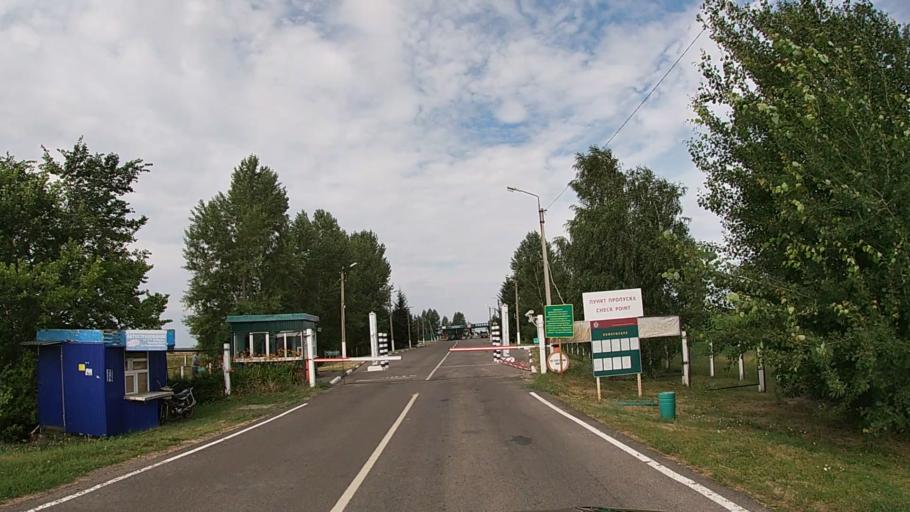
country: UA
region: Sumy
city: Krasnopillya
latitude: 50.8138
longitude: 35.4177
